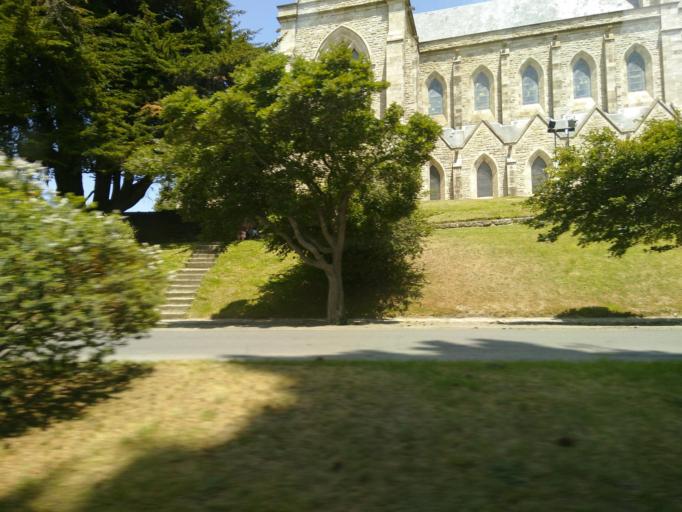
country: AR
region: Rio Negro
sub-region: Departamento de Bariloche
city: San Carlos de Bariloche
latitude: -41.1324
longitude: -71.3024
